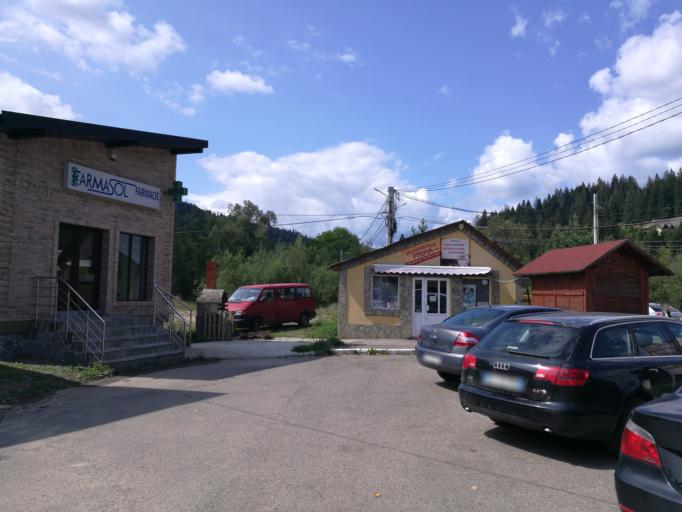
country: RO
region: Suceava
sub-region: Comuna Sucevita
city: Sucevita
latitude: 47.7794
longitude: 25.7098
